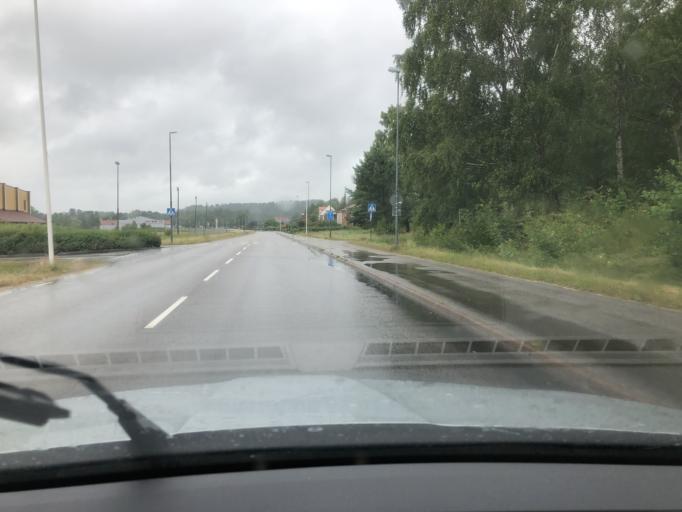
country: SE
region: Blekinge
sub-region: Olofstroms Kommun
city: Olofstroem
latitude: 56.2708
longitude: 14.5307
